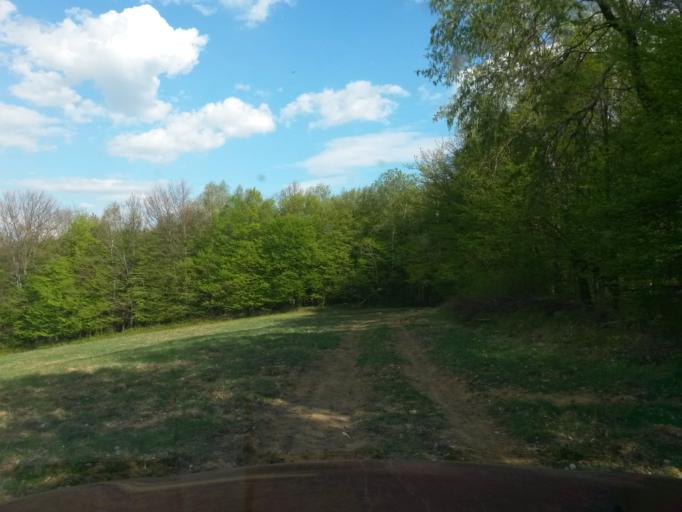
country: SK
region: Presovsky
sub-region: Okres Presov
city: Presov
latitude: 48.9498
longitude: 21.1488
